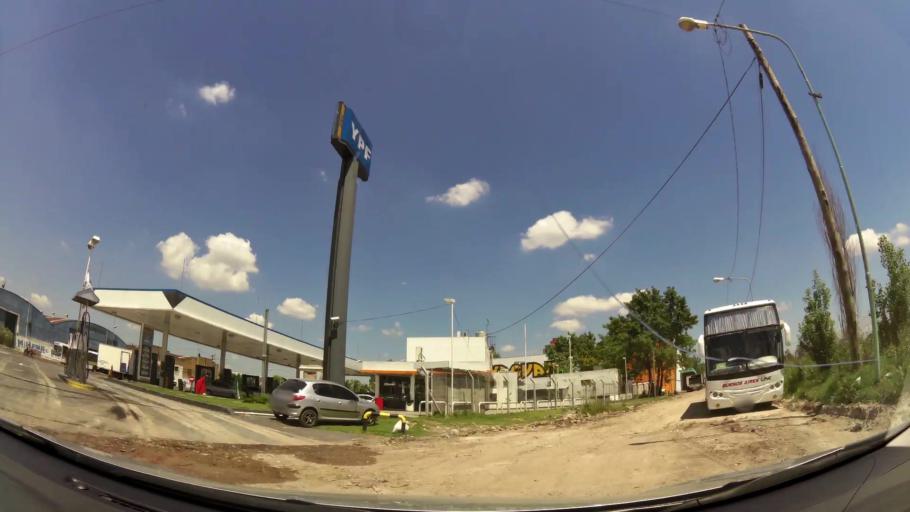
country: AR
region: Buenos Aires
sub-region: Partido de Tigre
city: Tigre
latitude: -34.4409
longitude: -58.5838
